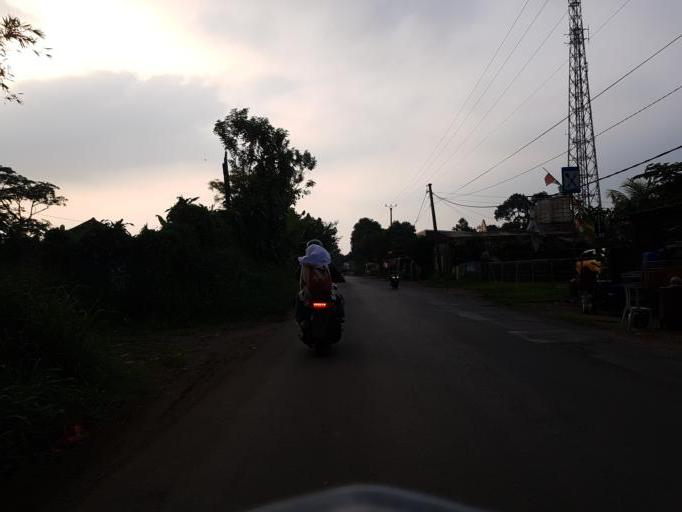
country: ID
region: West Java
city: Parung
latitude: -6.4698
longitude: 106.7172
